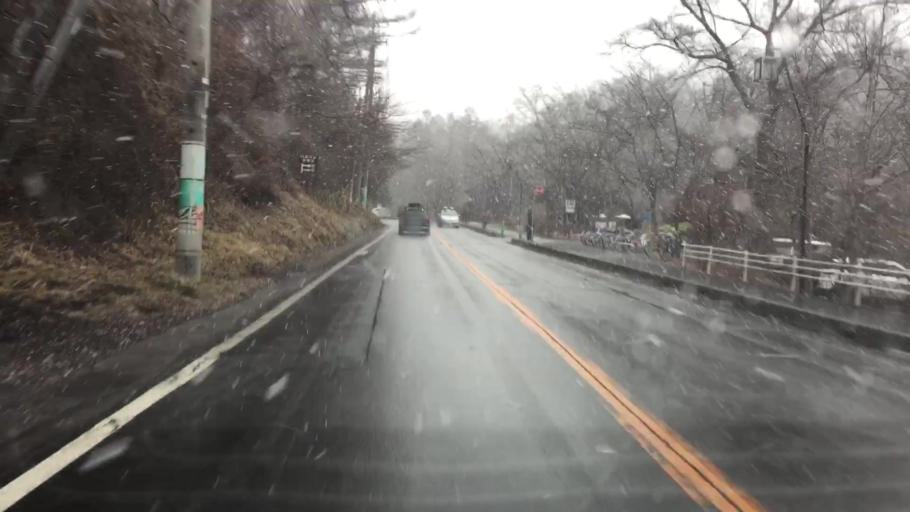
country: JP
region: Nagano
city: Komoro
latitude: 36.3582
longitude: 138.5902
